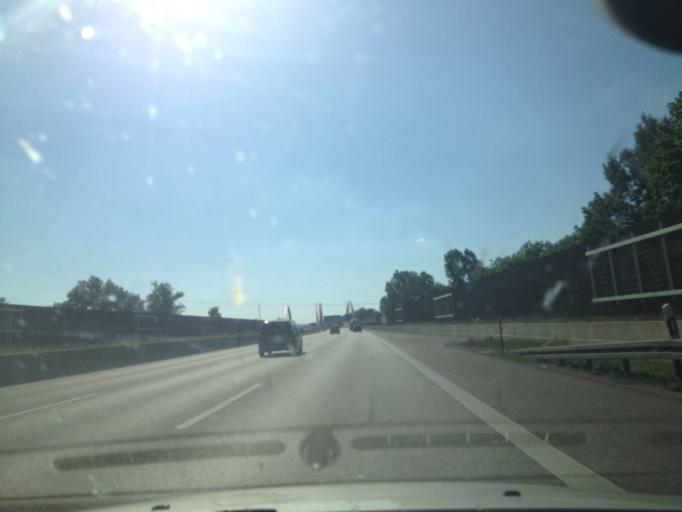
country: DE
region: Bavaria
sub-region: Swabia
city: Gersthofen
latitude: 48.4139
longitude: 10.8950
